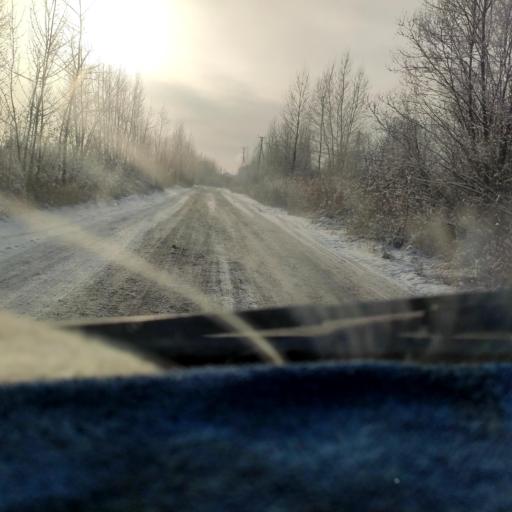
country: RU
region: Bashkortostan
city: Avdon
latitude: 54.6722
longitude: 55.8158
